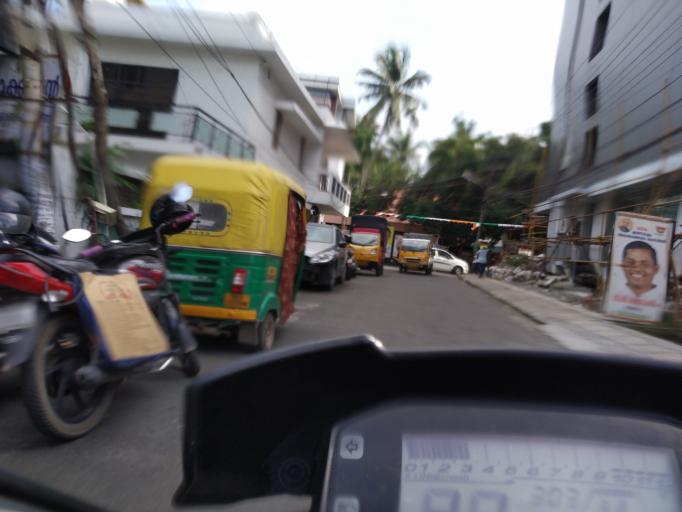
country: IN
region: Kerala
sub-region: Ernakulam
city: Cochin
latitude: 9.9855
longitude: 76.2860
